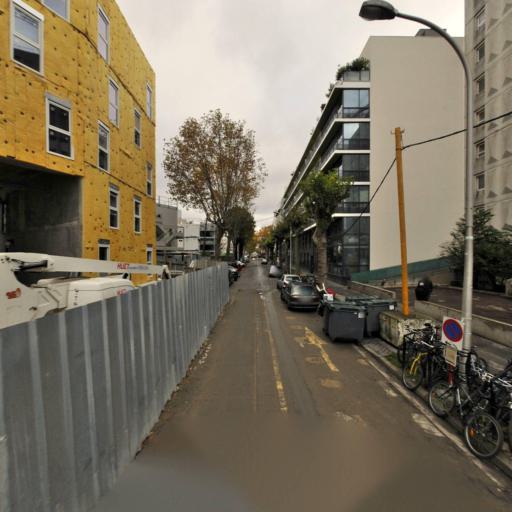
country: FR
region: Ile-de-France
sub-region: Departement des Hauts-de-Seine
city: Boulogne-Billancourt
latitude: 48.8258
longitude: 2.2419
